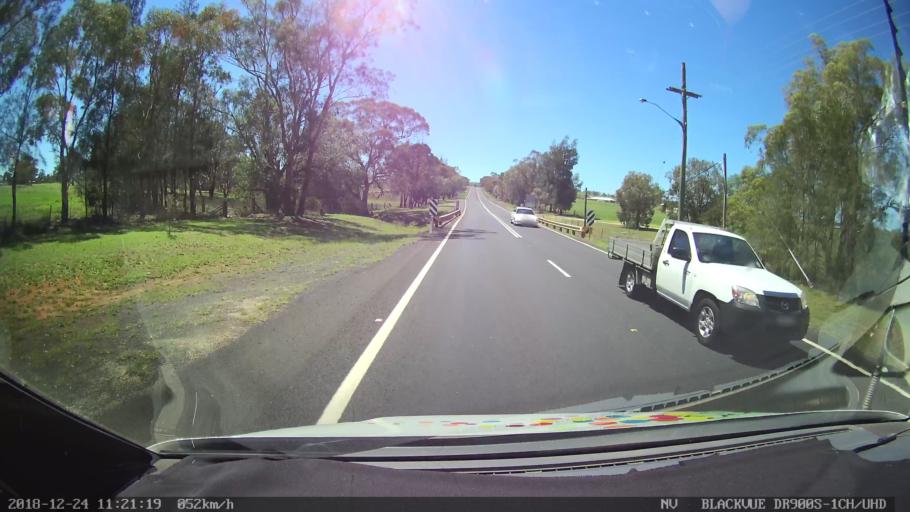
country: AU
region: New South Wales
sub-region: Upper Hunter Shire
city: Merriwa
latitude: -32.1425
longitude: 150.3693
